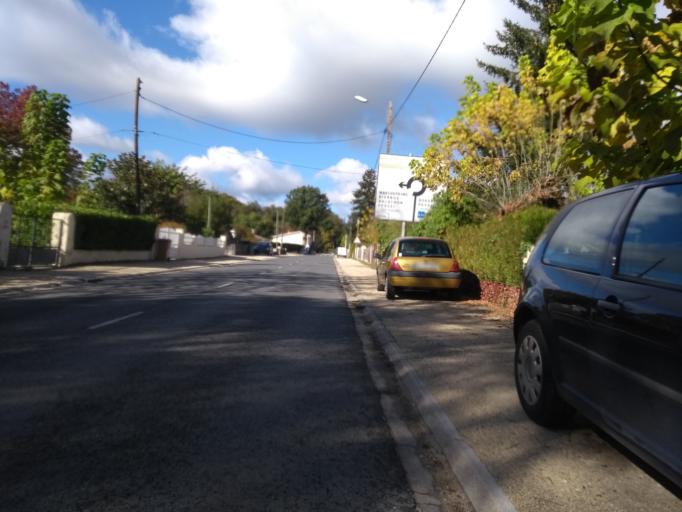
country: FR
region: Aquitaine
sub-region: Departement de la Gironde
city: Saint-Aubin-de-Medoc
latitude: 44.7737
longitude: -0.7037
